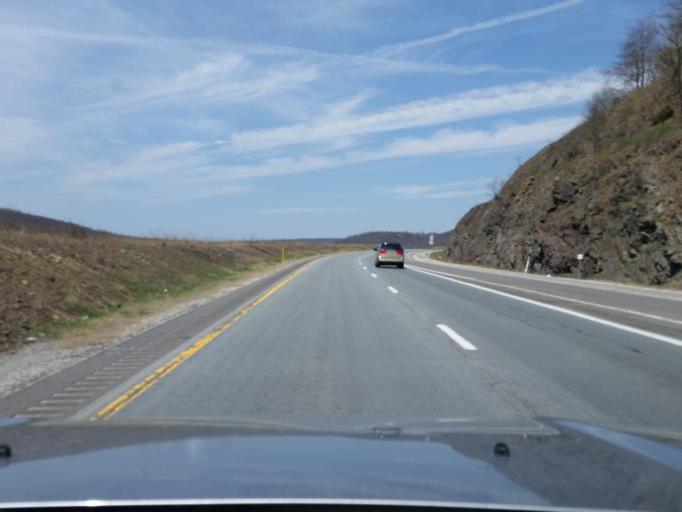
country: US
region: Pennsylvania
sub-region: Perry County
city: Duncannon
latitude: 40.4527
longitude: -77.0228
